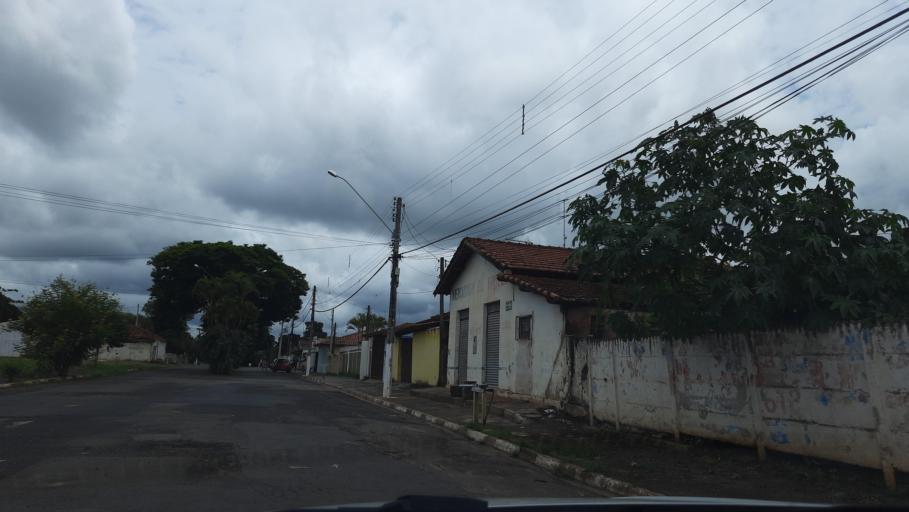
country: BR
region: Sao Paulo
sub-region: Casa Branca
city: Casa Branca
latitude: -21.7826
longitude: -47.0957
